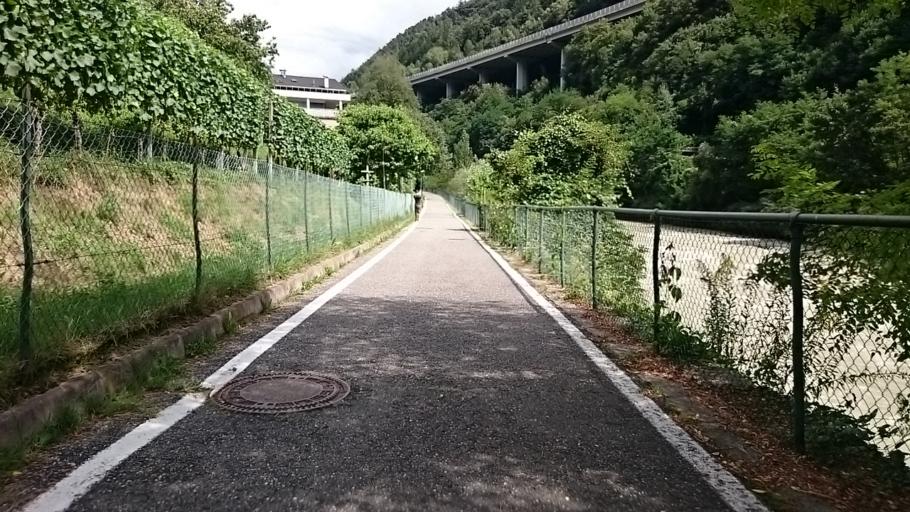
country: IT
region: Trentino-Alto Adige
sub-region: Bolzano
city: Chiusa
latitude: 46.6361
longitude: 11.5593
